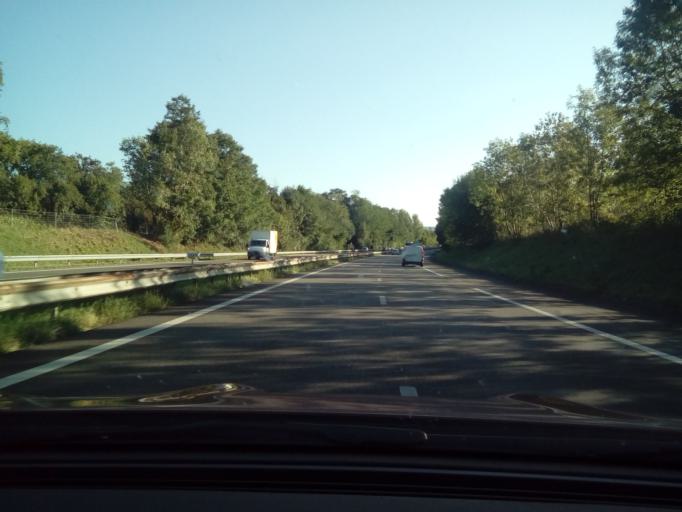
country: FR
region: Rhone-Alpes
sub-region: Departement de la Savoie
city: La Biolle
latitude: 45.7451
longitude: 5.9290
